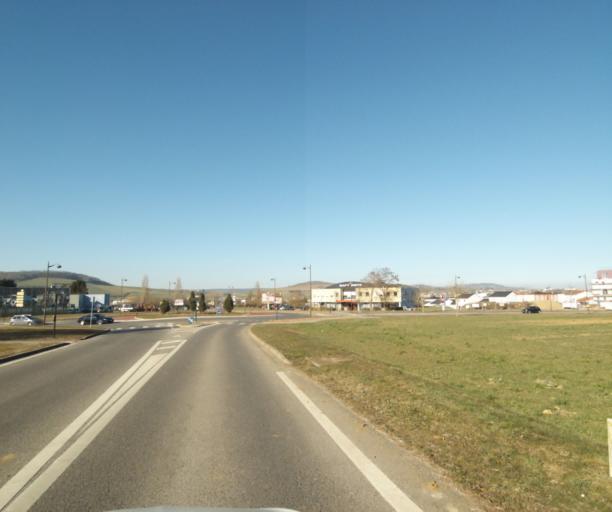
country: FR
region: Lorraine
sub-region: Departement de Meurthe-et-Moselle
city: Saulxures-les-Nancy
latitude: 48.6986
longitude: 6.2485
